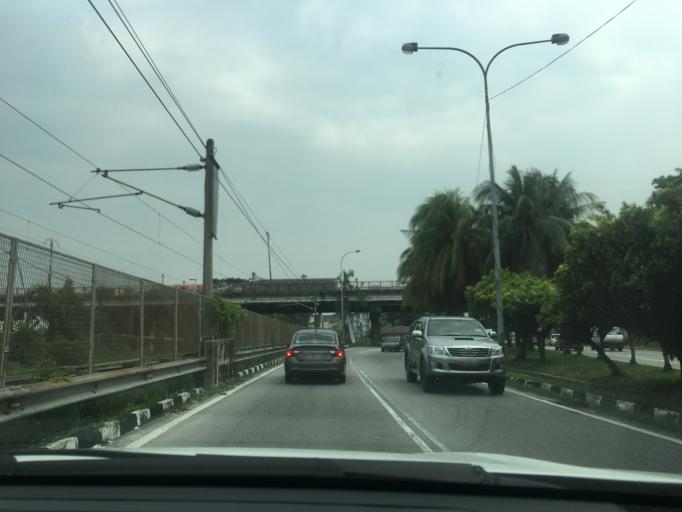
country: MY
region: Selangor
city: Klang
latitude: 3.0457
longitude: 101.4454
